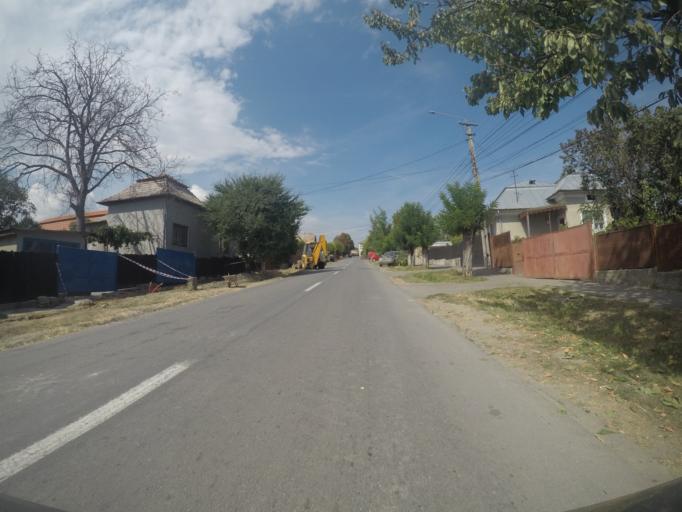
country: RO
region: Cluj
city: Turda
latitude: 46.5770
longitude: 23.7944
